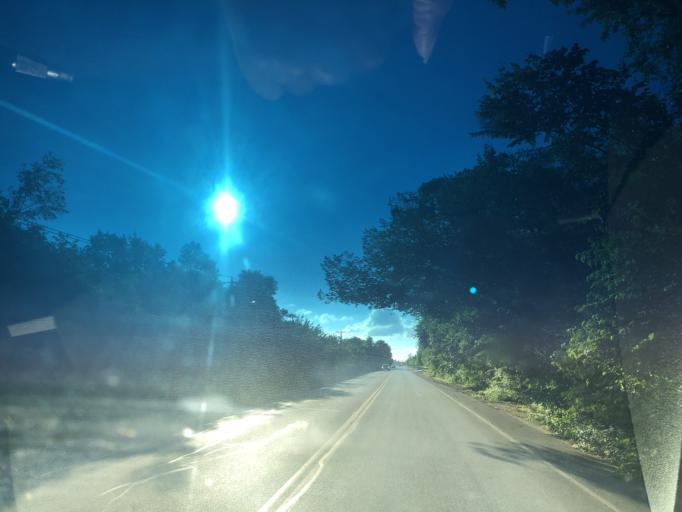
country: US
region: Texas
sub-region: Dallas County
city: Grand Prairie
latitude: 32.7778
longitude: -97.0011
